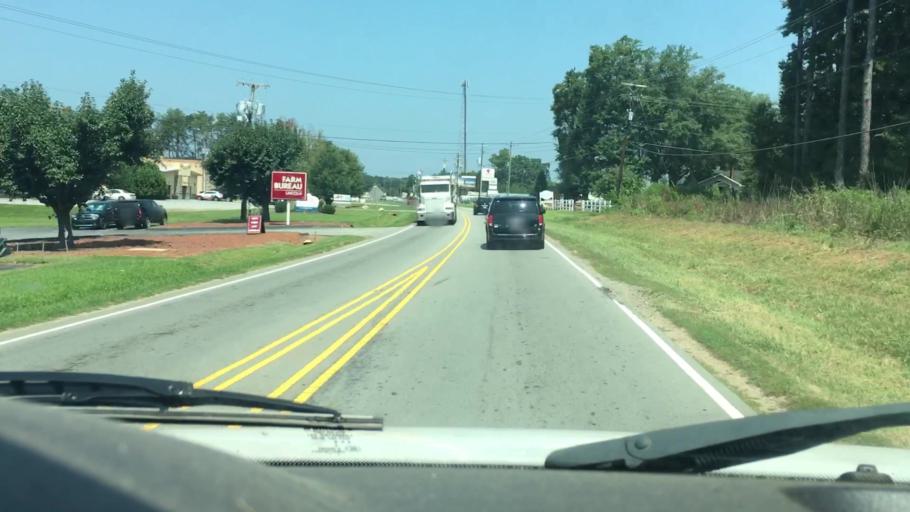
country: US
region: North Carolina
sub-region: Lincoln County
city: Westport
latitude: 35.4799
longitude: -80.9934
